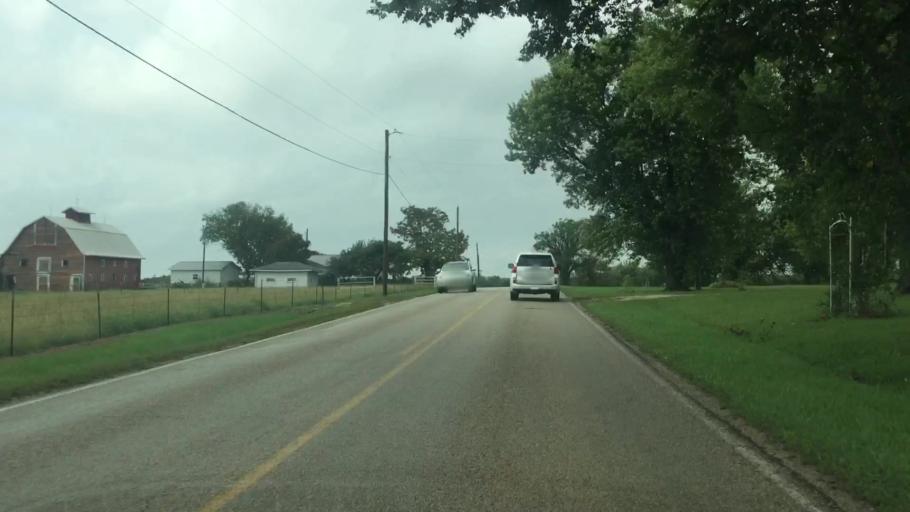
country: US
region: Kansas
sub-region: Allen County
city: Iola
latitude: 37.8857
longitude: -95.4233
